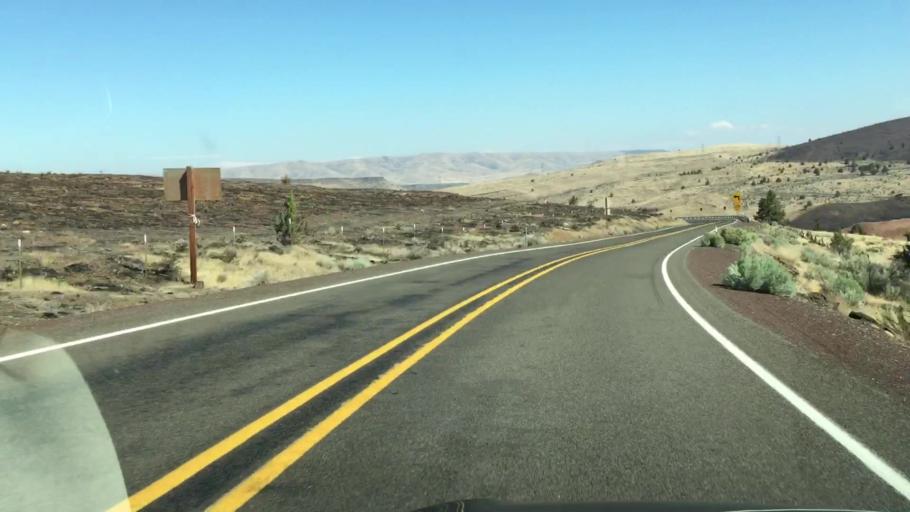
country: US
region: Oregon
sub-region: Wasco County
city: The Dalles
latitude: 45.1639
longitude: -121.0726
